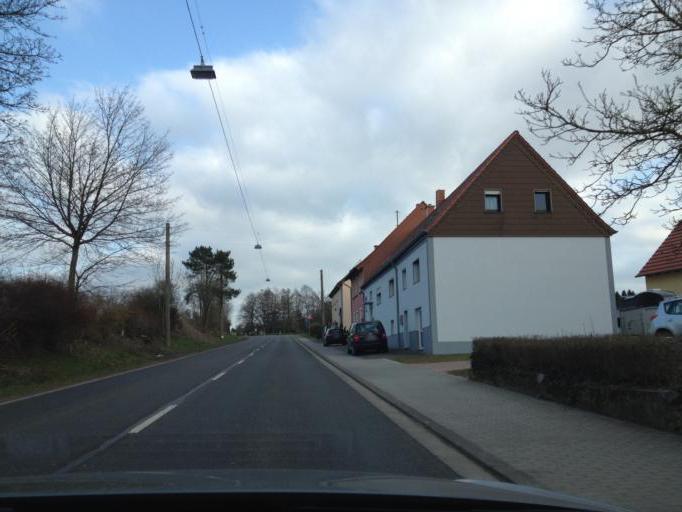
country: DE
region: Saarland
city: Oberthal
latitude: 49.4698
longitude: 7.1054
